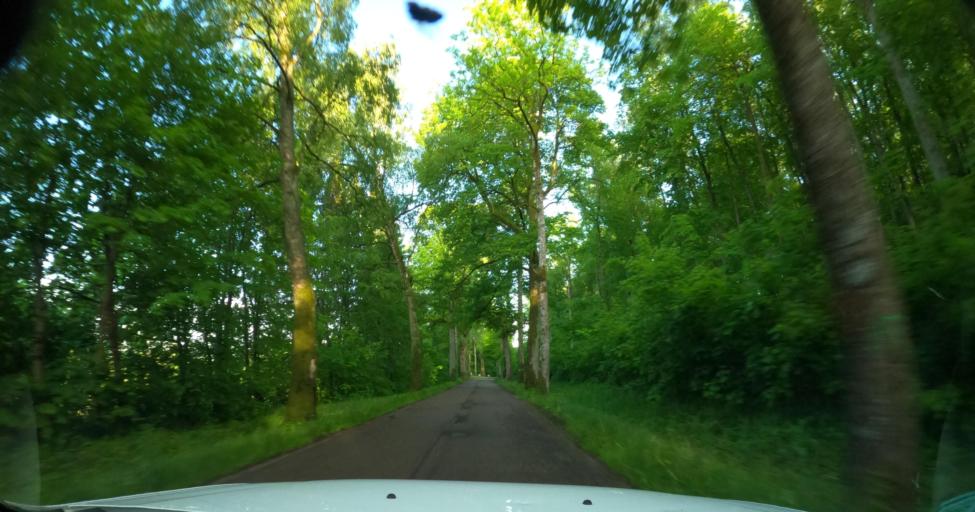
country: PL
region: Warmian-Masurian Voivodeship
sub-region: Powiat braniewski
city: Pieniezno
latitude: 54.2151
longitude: 20.0383
